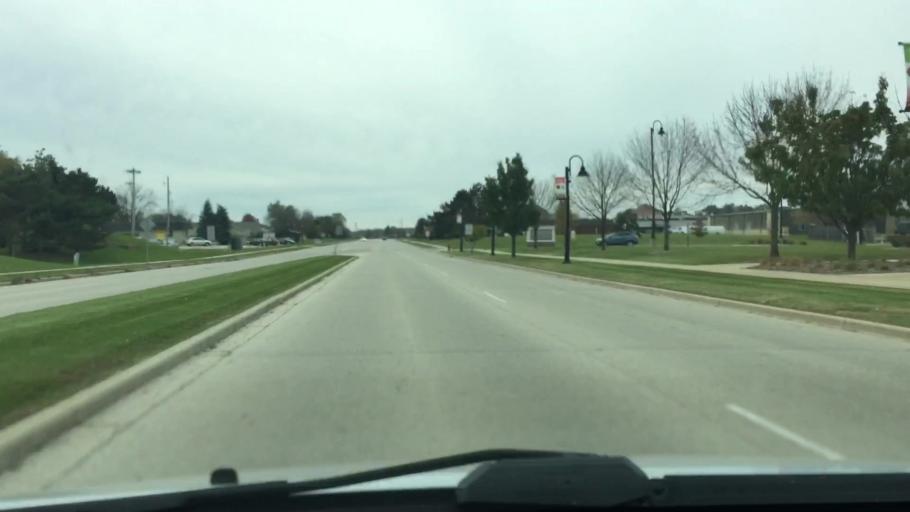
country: US
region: Wisconsin
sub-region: Waukesha County
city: New Berlin
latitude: 42.9704
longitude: -88.1175
